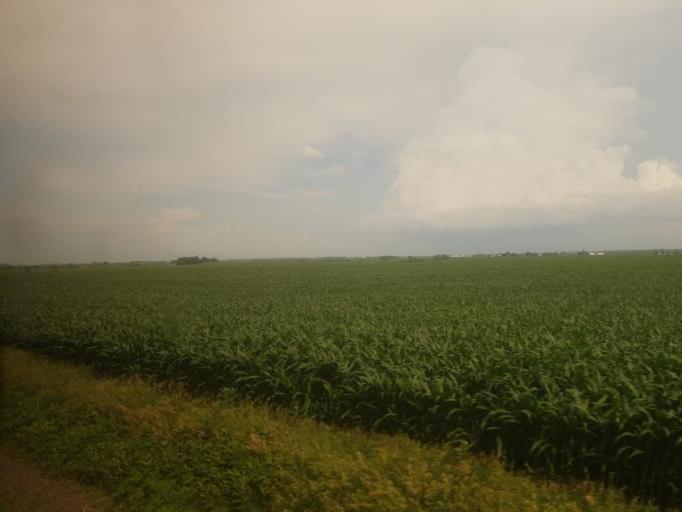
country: US
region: Illinois
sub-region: Henry County
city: Galva
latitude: 41.1269
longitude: -90.1319
